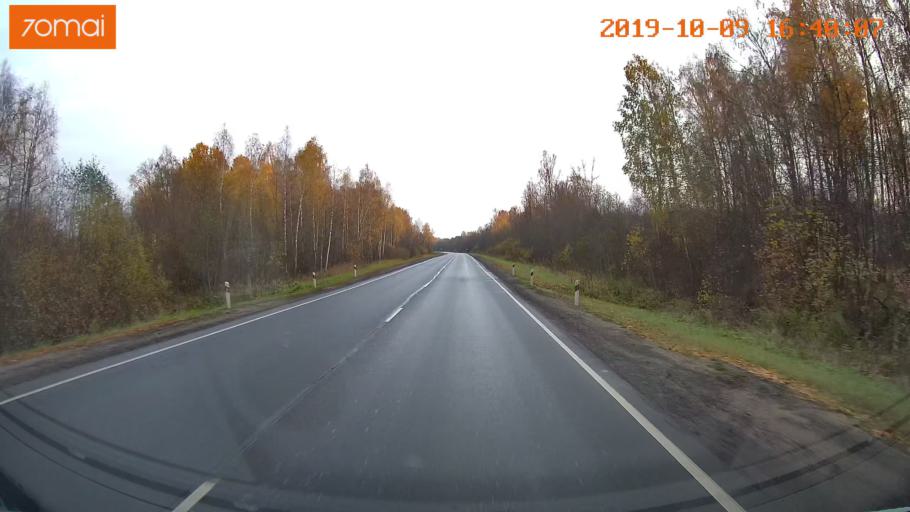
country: RU
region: Kostroma
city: Volgorechensk
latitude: 57.4882
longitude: 41.0566
